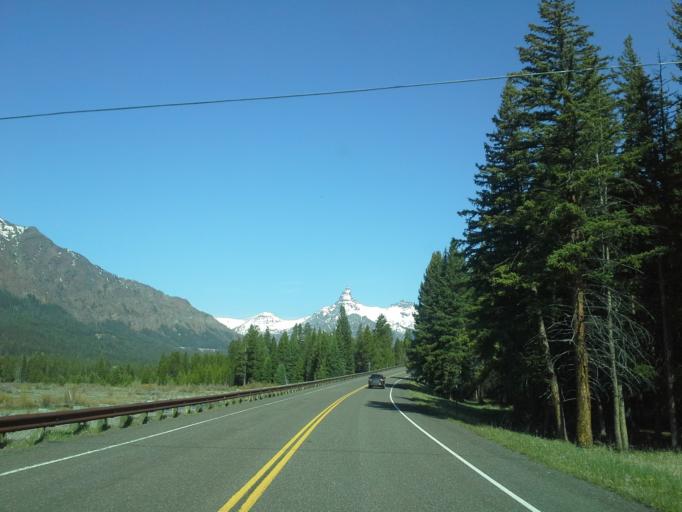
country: US
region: Montana
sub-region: Carbon County
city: Red Lodge
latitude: 44.9369
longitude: -109.7640
